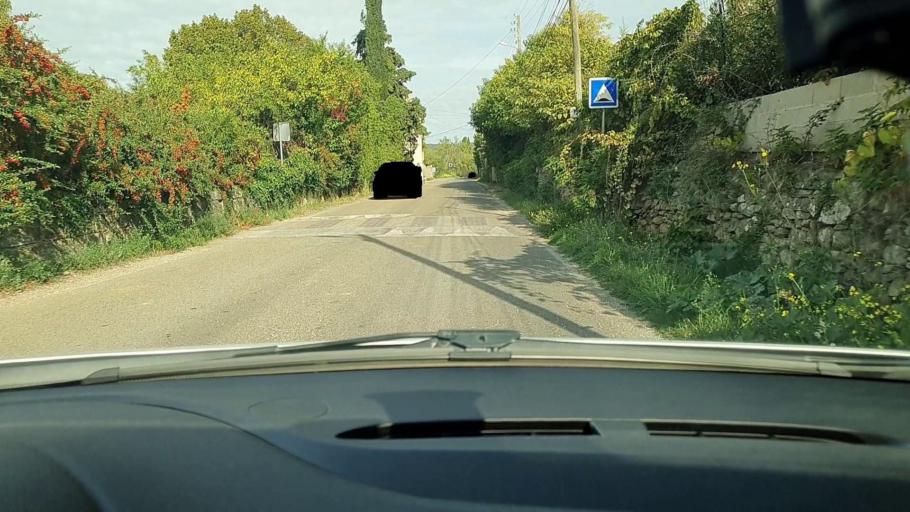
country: FR
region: Languedoc-Roussillon
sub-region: Departement du Gard
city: Saint-Quentin-la-Poterie
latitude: 44.0493
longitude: 4.4371
